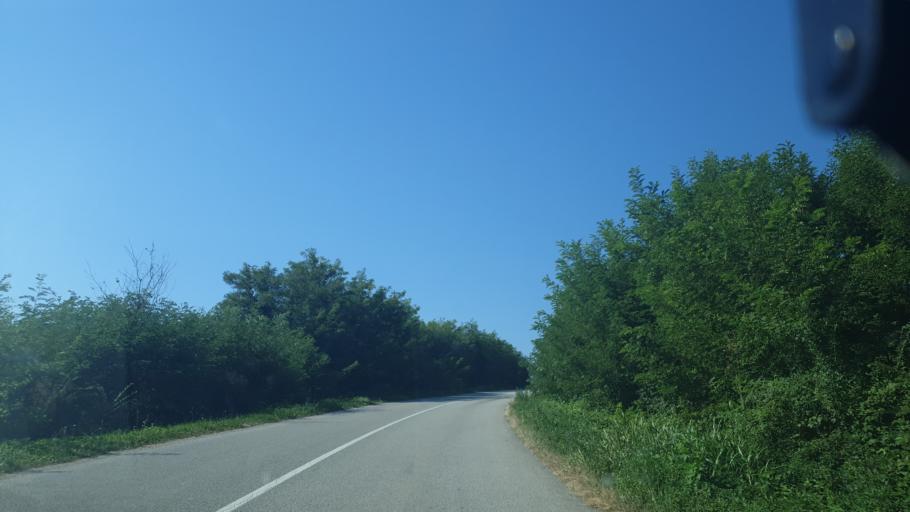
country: RS
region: Central Serbia
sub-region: Kolubarski Okrug
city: Mionica
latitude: 44.2795
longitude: 20.1094
